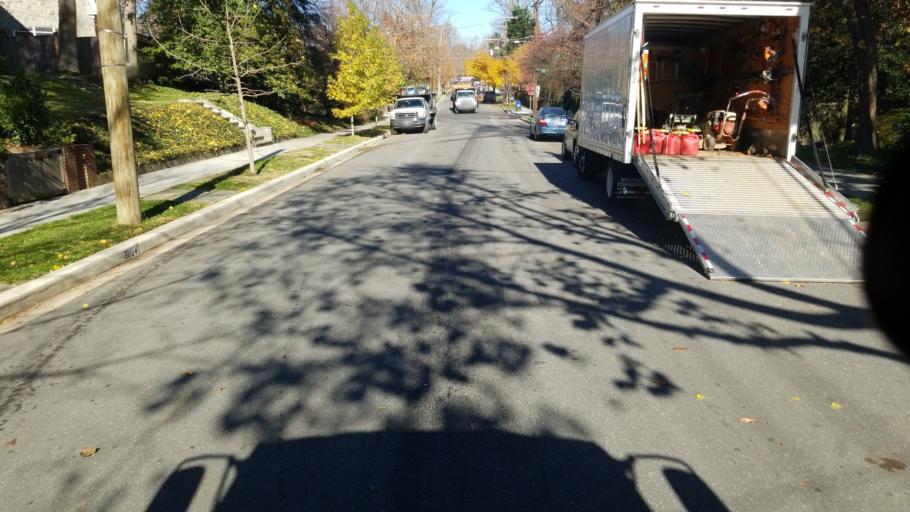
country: US
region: Maryland
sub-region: Montgomery County
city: Friendship Village
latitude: 38.9295
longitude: -77.0862
